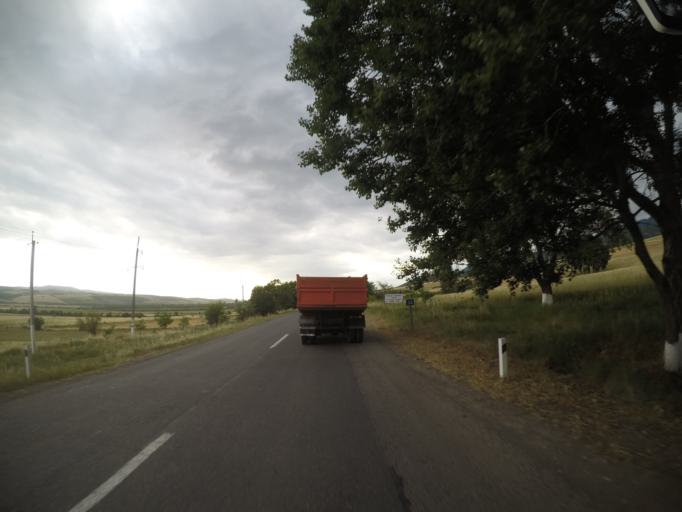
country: AZ
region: Ismayilli
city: Ismayilli
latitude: 40.7442
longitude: 48.2516
